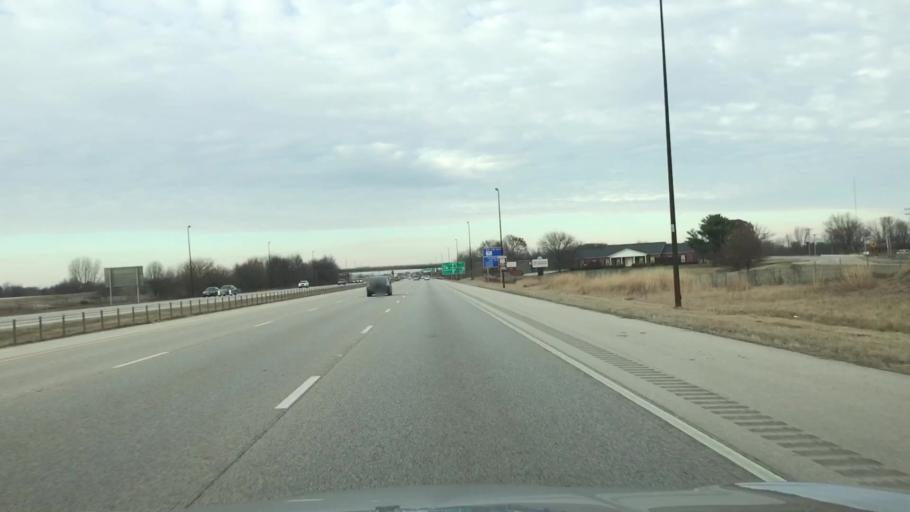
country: US
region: Illinois
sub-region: Sangamon County
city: Southern View
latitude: 39.7247
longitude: -89.6439
